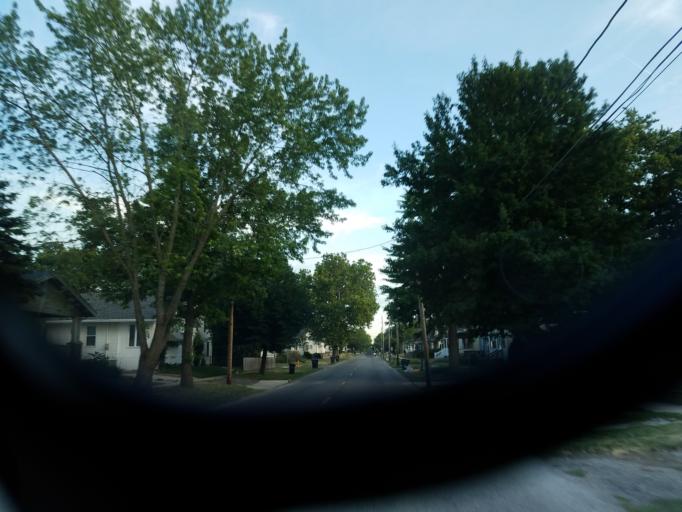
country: US
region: Illinois
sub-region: McLean County
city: Bloomington
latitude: 40.4691
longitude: -88.9941
